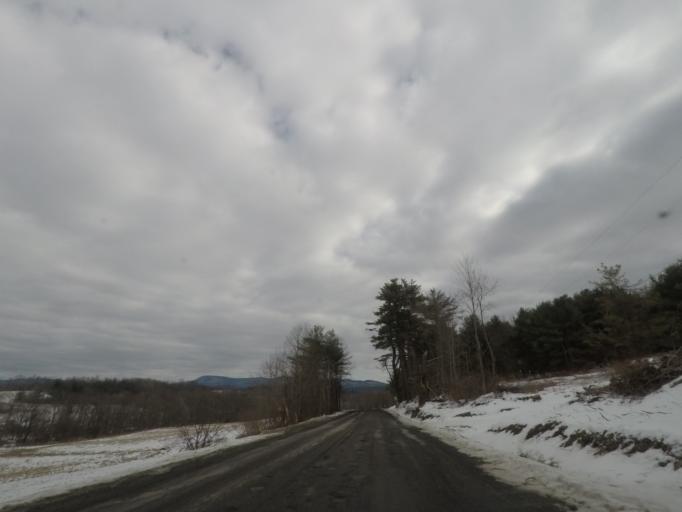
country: US
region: New York
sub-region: Rensselaer County
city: Hoosick Falls
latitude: 42.8634
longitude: -73.3620
